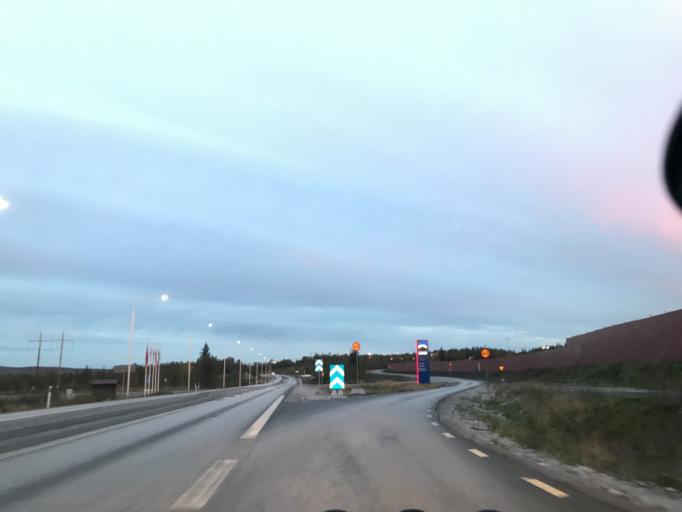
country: SE
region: Norrbotten
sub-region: Gallivare Kommun
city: Malmberget
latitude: 67.6533
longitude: 21.0149
